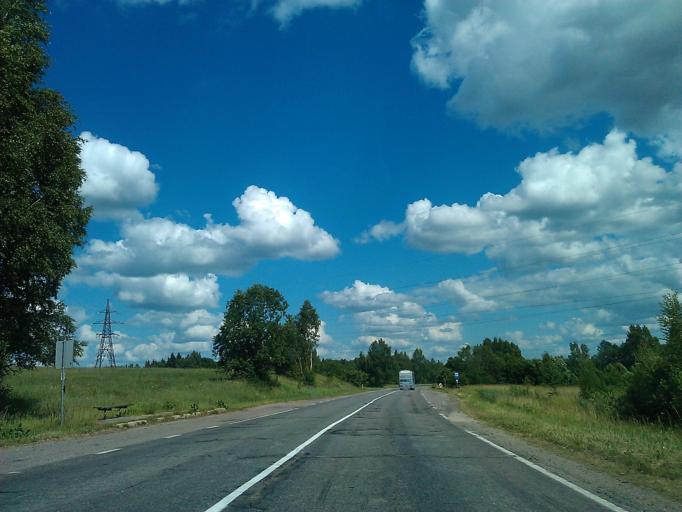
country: LV
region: Rezekne
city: Rezekne
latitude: 56.5492
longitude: 27.3295
